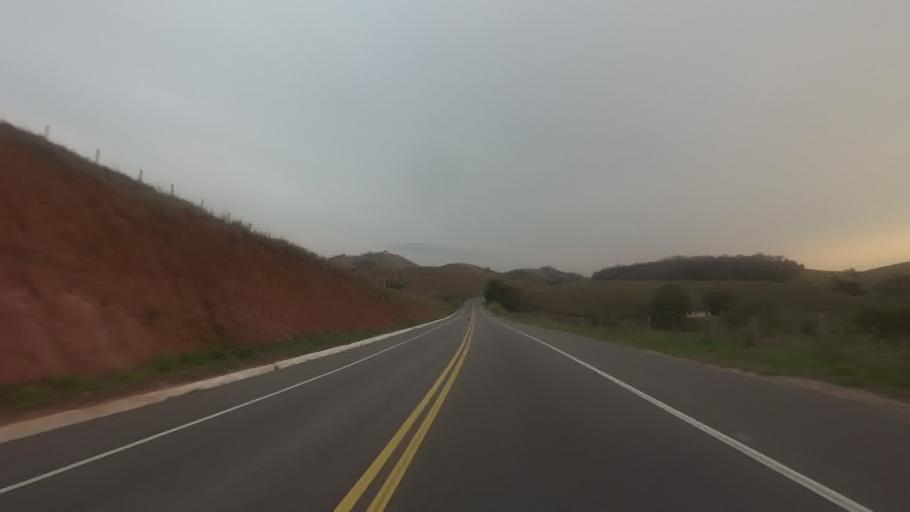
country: BR
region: Minas Gerais
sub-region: Recreio
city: Recreio
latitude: -21.7026
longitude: -42.4220
